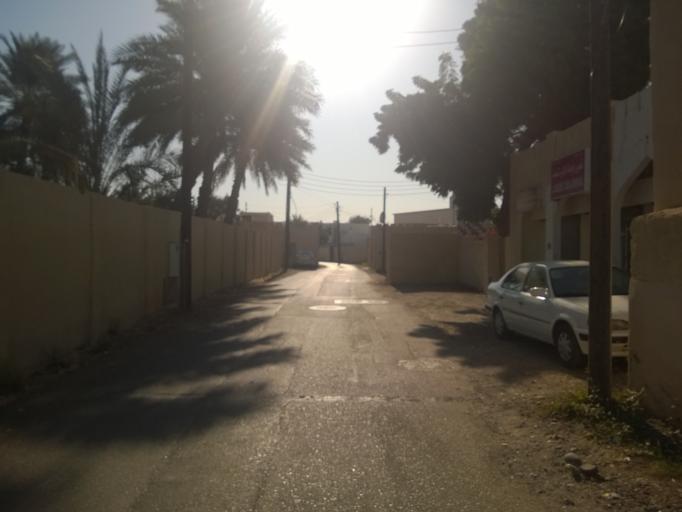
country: OM
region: Muhafazat Masqat
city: As Sib al Jadidah
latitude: 23.6672
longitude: 58.1847
